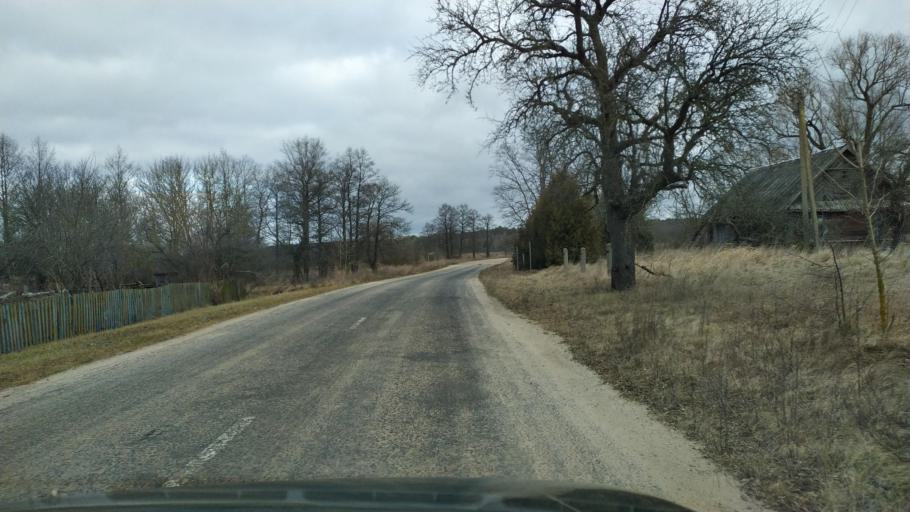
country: BY
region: Brest
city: Kamyanyets
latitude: 52.4173
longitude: 23.9322
